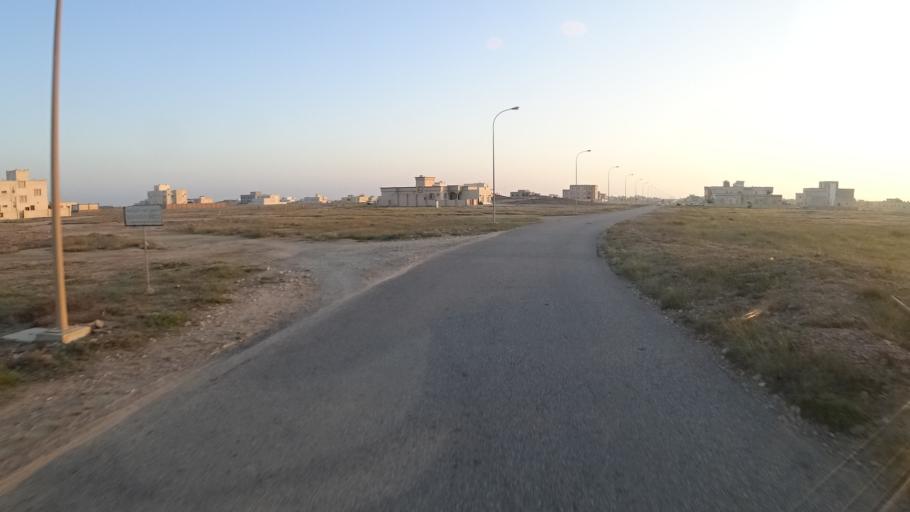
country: OM
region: Zufar
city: Salalah
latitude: 16.9940
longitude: 54.7196
